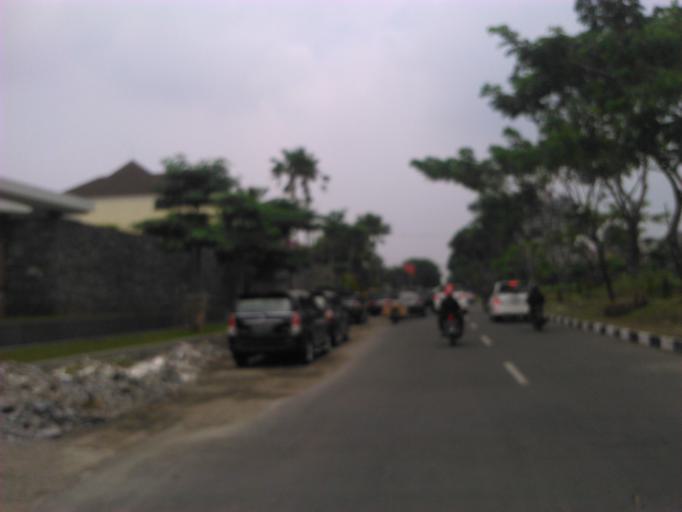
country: ID
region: East Java
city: Mulyorejo
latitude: -7.2800
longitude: 112.7866
